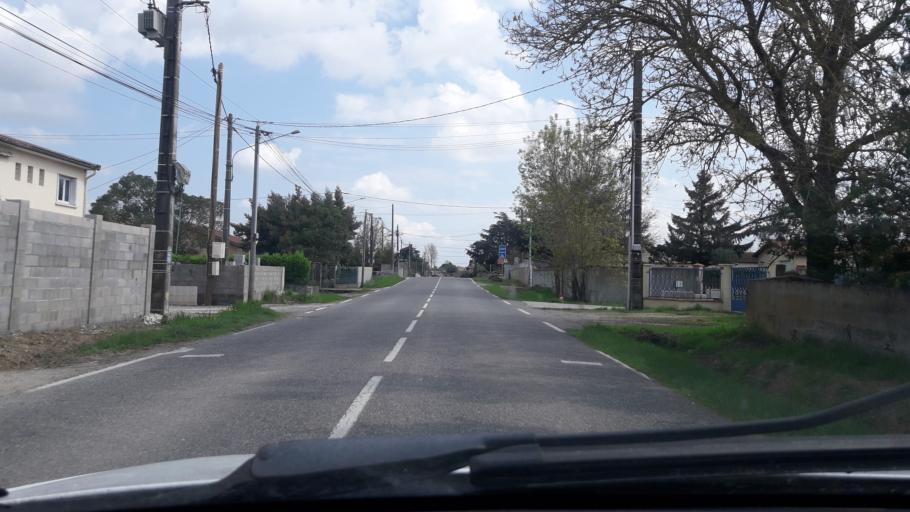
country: FR
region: Midi-Pyrenees
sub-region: Departement de la Haute-Garonne
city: Seysses
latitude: 43.4989
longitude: 1.2939
